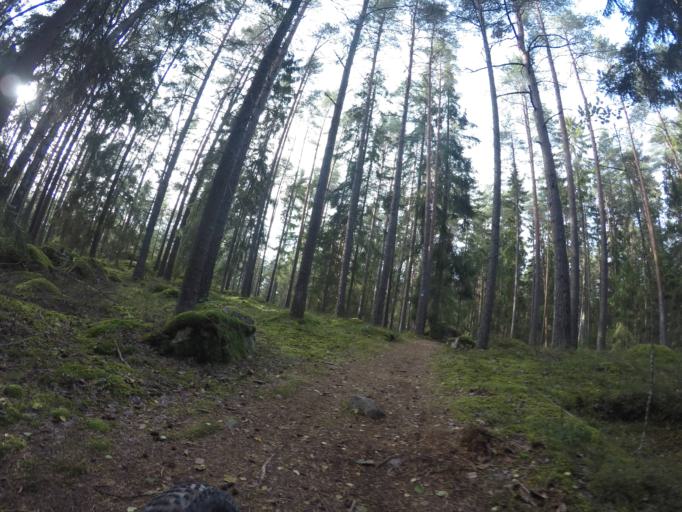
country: SE
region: Vaestmanland
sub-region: Kopings Kommun
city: Koping
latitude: 59.5331
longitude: 15.9974
